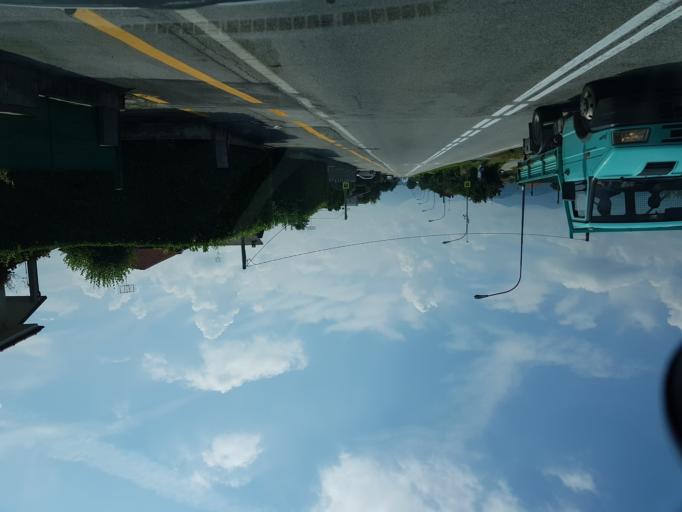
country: IT
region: Piedmont
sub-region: Provincia di Cuneo
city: Vignolo
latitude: 44.3643
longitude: 7.4745
